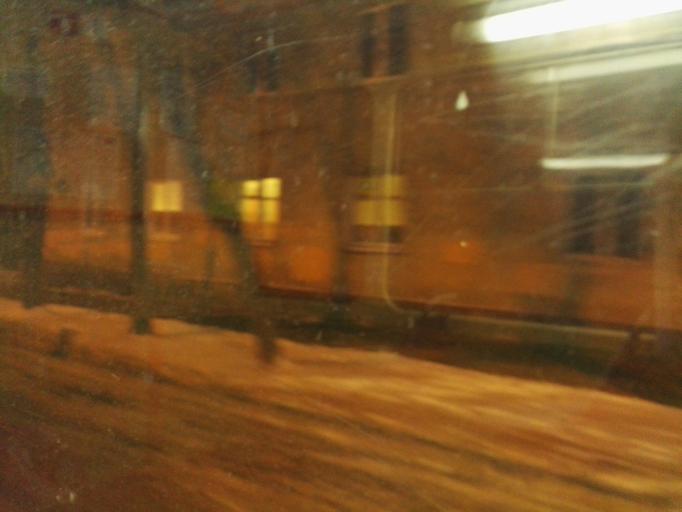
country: RU
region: Tula
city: Mendeleyevskiy
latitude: 54.1694
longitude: 37.5834
